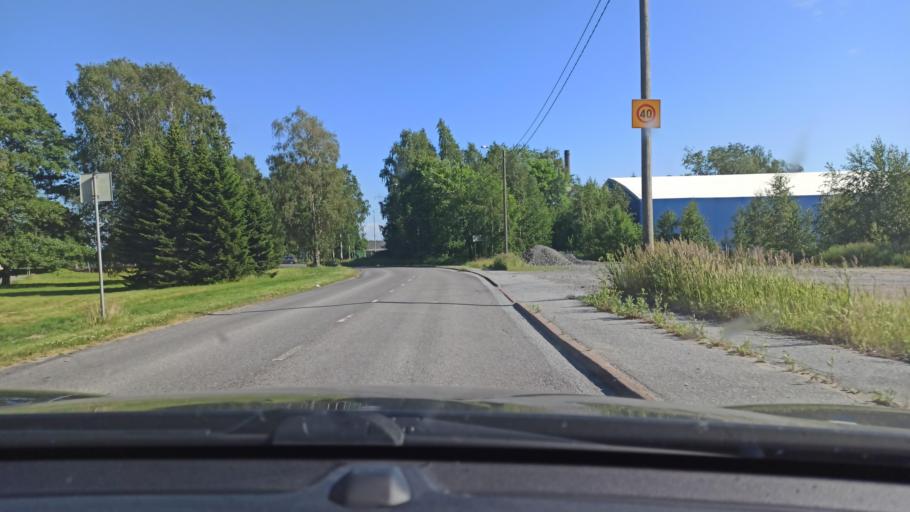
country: FI
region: Satakunta
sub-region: Pori
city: Pori
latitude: 61.4958
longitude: 21.8138
